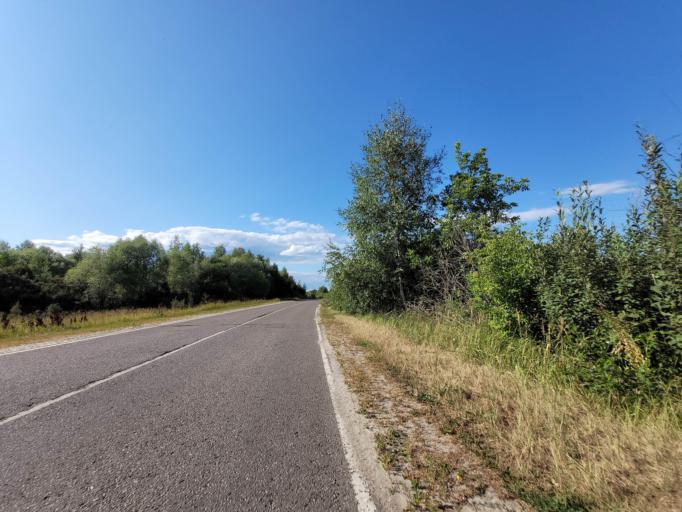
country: RU
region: Moskovskaya
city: Konobeyevo
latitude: 55.4021
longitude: 38.7088
